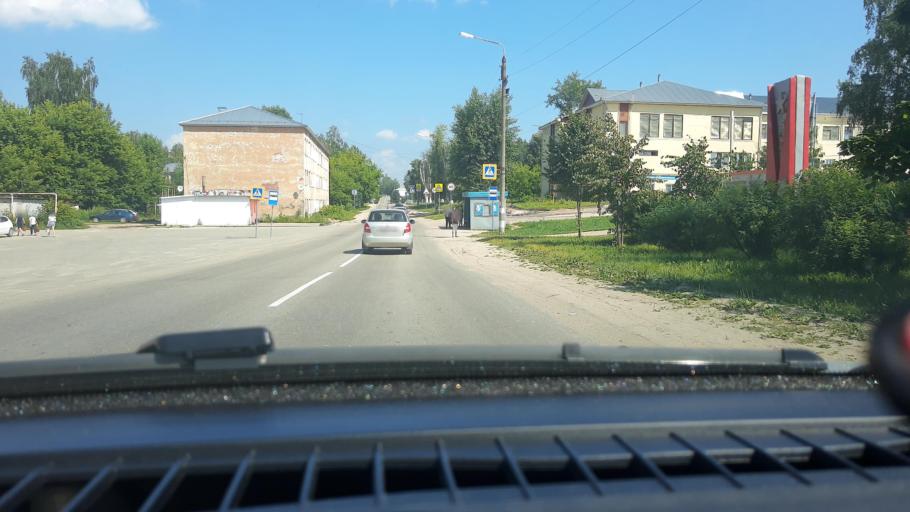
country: RU
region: Nizjnij Novgorod
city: Afonino
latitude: 56.2839
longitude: 44.1906
